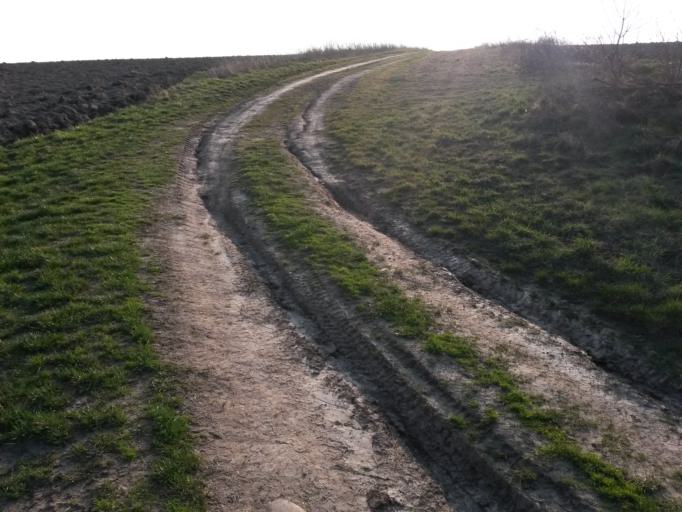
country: HU
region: Pest
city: Perbal
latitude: 47.5980
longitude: 18.7836
